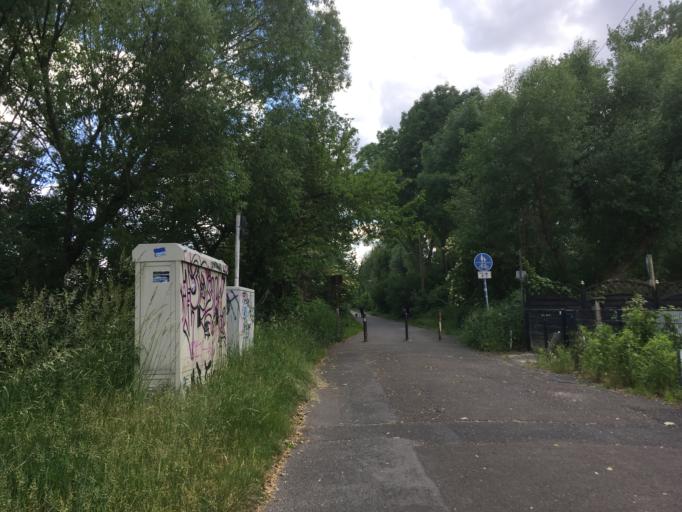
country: DE
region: Berlin
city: Wartenberg
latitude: 52.5733
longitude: 13.5307
